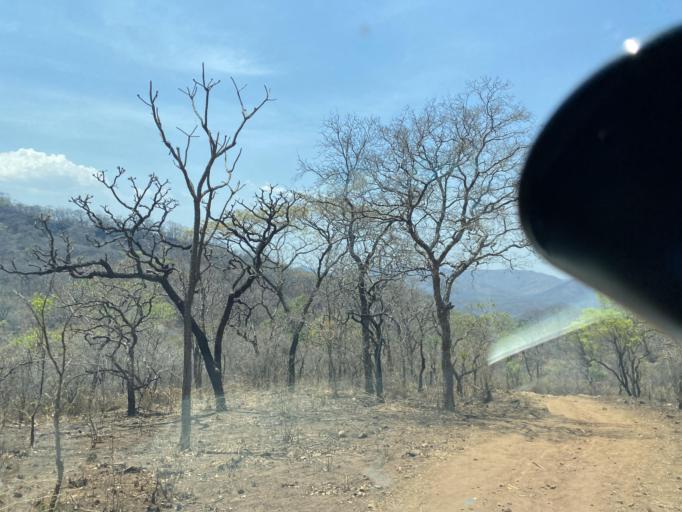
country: ZM
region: Lusaka
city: Kafue
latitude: -15.8027
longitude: 28.4496
